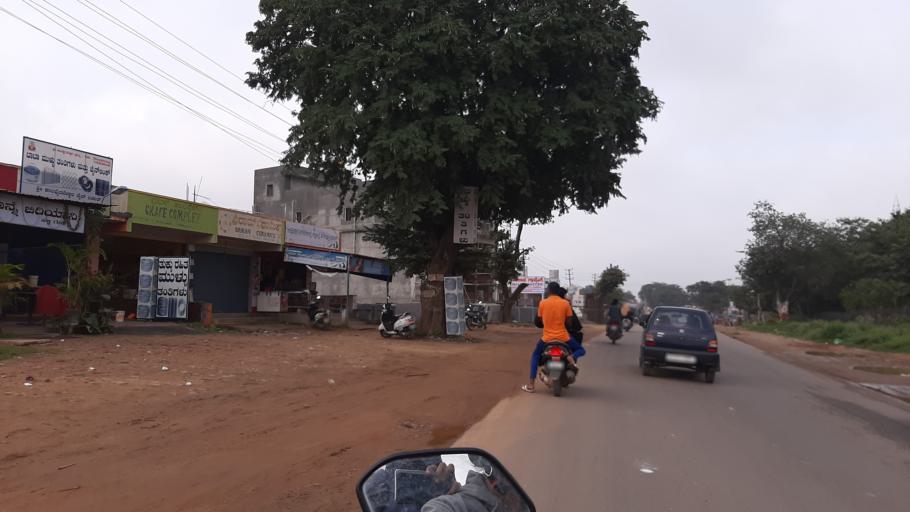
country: IN
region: Karnataka
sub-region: Bangalore Rural
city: Nelamangala
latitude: 12.9858
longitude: 77.4465
